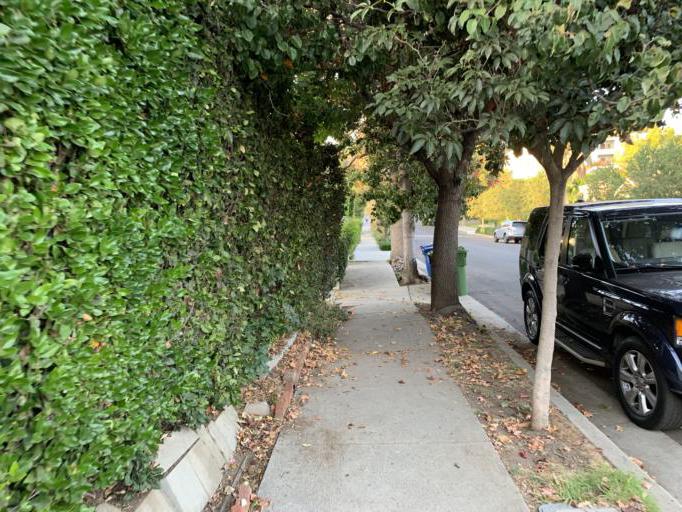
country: US
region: California
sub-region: Los Angeles County
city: West Hollywood
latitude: 34.1003
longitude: -118.3551
